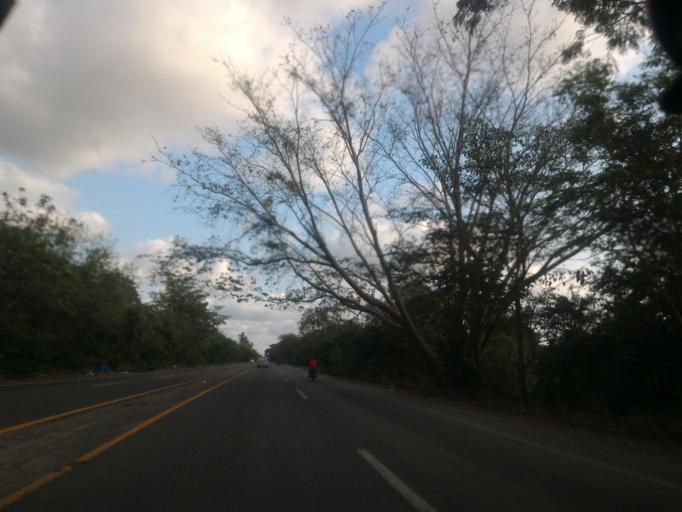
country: MX
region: Colima
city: Tecoman
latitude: 18.8863
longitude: -103.8519
